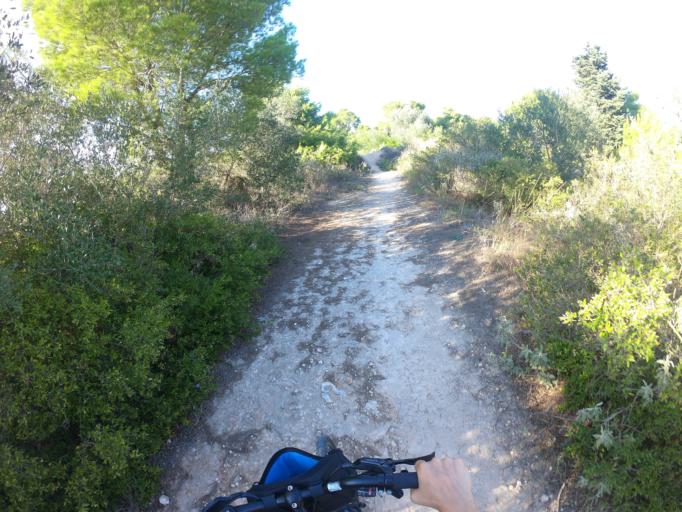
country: IT
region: Apulia
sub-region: Provincia di Lecce
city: Supersano
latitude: 40.0422
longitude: 18.2108
